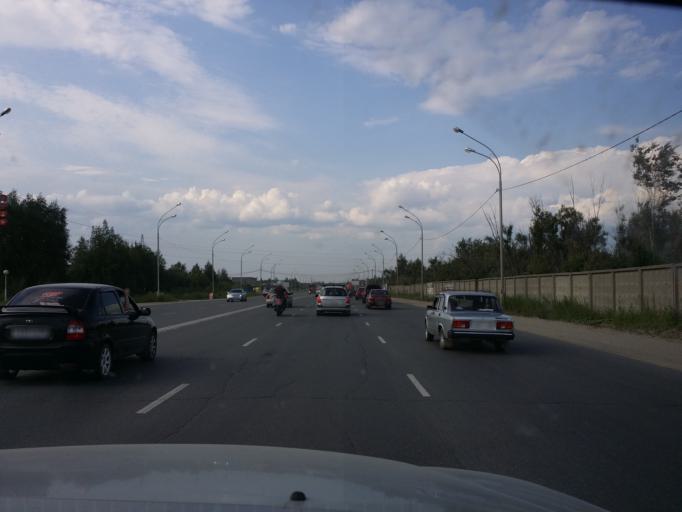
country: RU
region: Khanty-Mansiyskiy Avtonomnyy Okrug
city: Nizhnevartovsk
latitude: 60.9571
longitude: 76.5303
